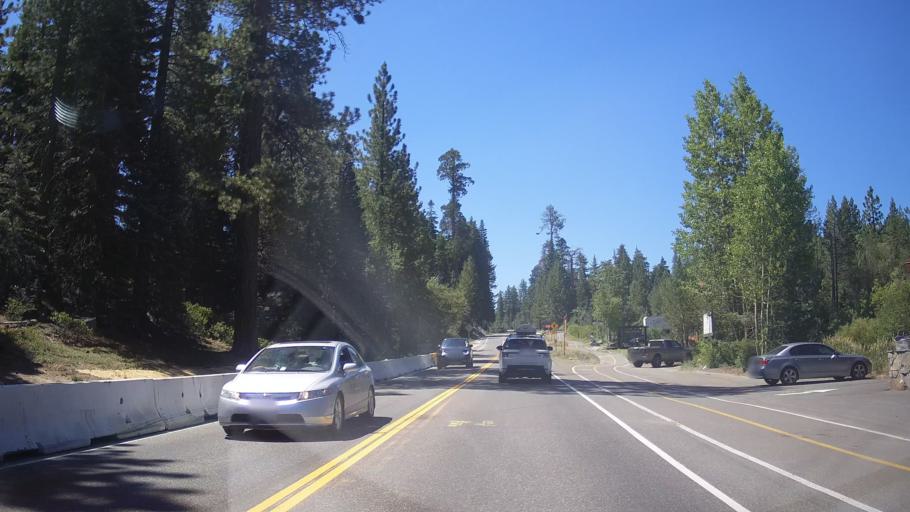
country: US
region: California
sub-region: Placer County
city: Sunnyside-Tahoe City
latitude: 39.1619
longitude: -120.1448
